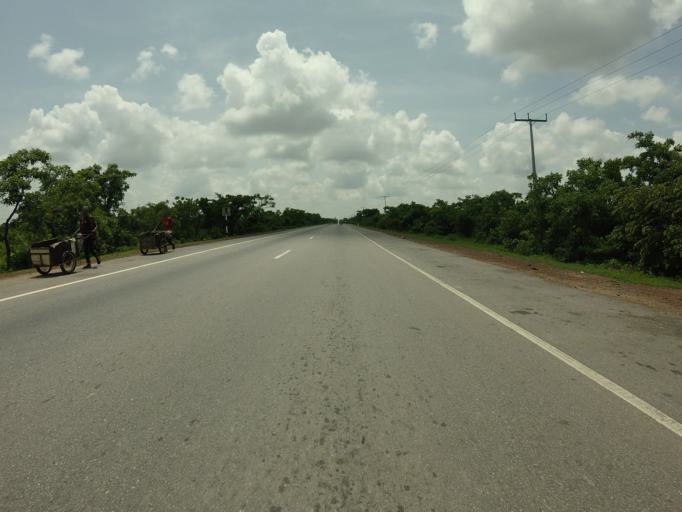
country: GH
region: Northern
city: Tamale
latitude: 9.1892
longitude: -1.0953
